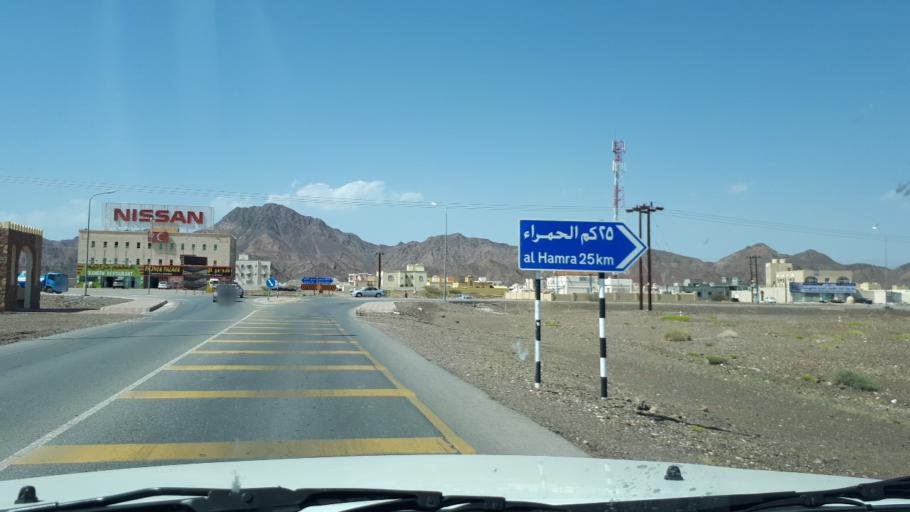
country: OM
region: Muhafazat ad Dakhiliyah
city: Bahla'
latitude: 22.9469
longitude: 57.2597
